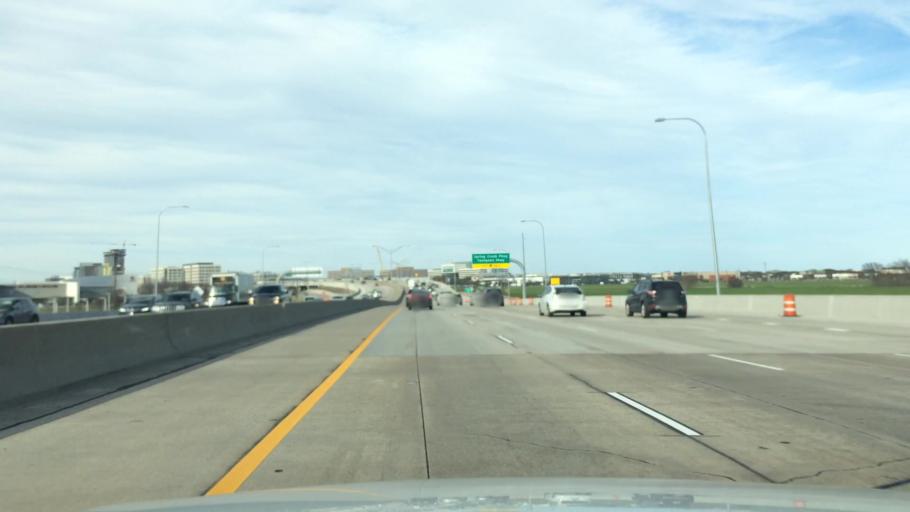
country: US
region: Texas
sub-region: Denton County
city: The Colony
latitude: 33.0597
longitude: -96.8281
